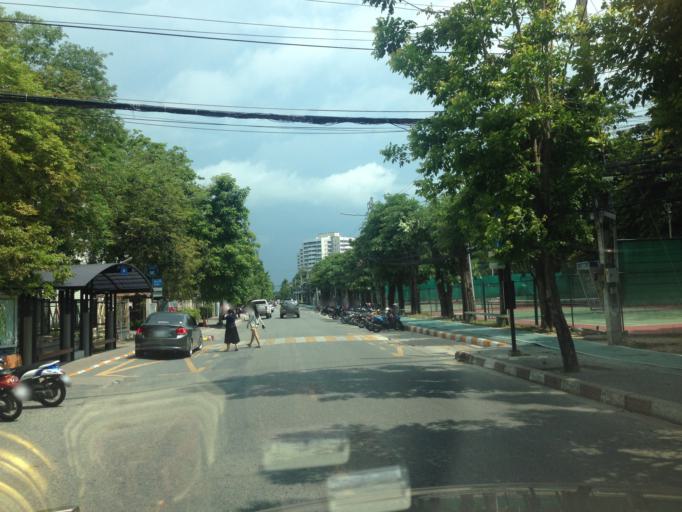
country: TH
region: Chon Buri
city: Chon Buri
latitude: 13.2773
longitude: 100.9279
